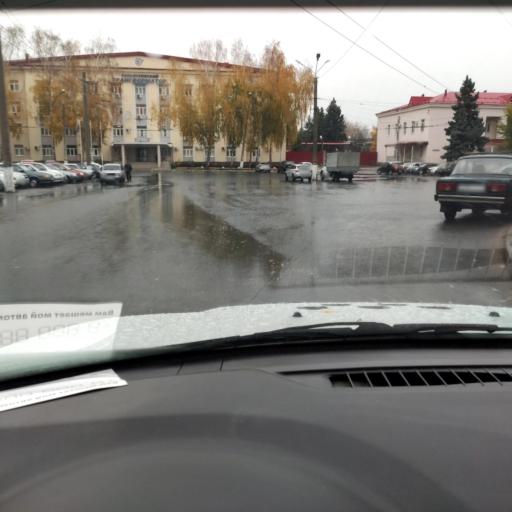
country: RU
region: Samara
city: Tol'yatti
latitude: 53.5182
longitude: 49.4573
